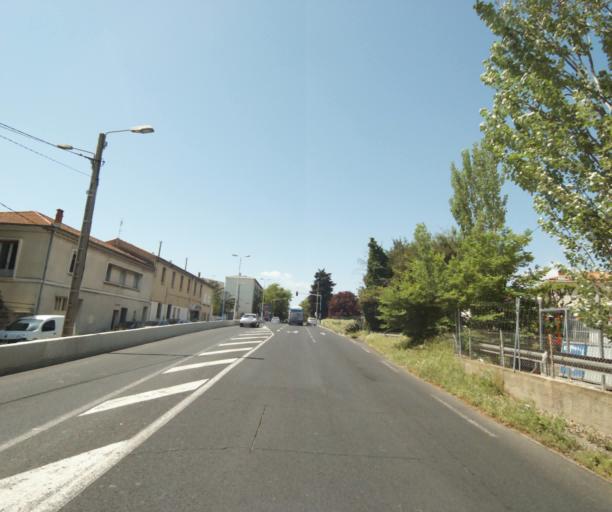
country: FR
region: Languedoc-Roussillon
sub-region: Departement de l'Herault
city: Montpellier
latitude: 43.5970
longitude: 3.8817
